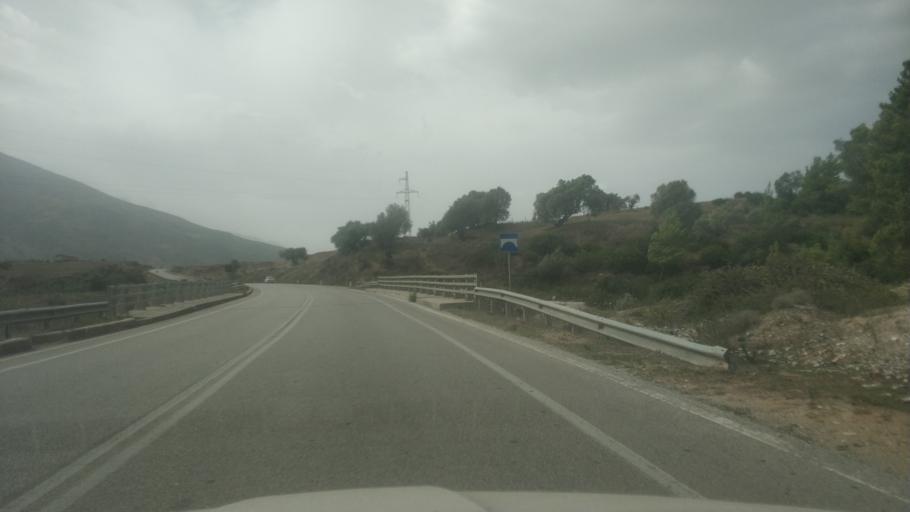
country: AL
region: Gjirokaster
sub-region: Rrethi i Tepelenes
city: Memaliaj
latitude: 40.3558
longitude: 19.9456
